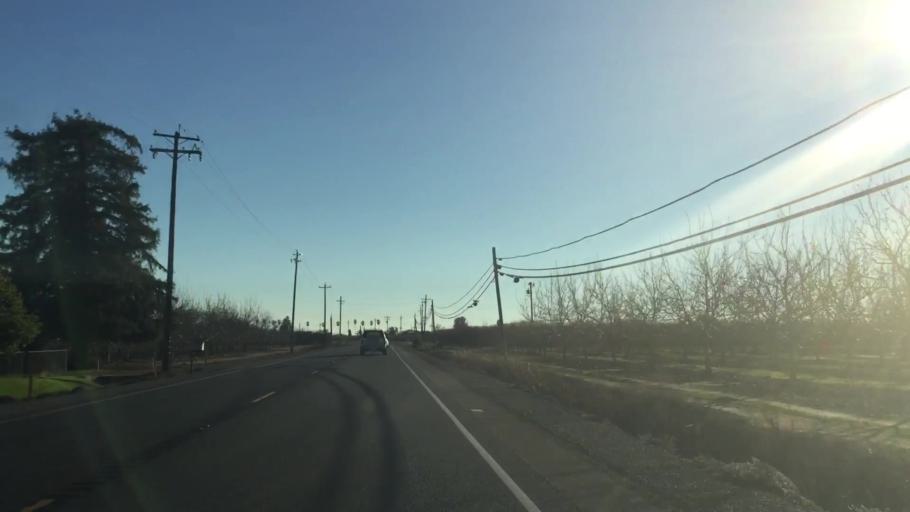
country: US
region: California
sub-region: Yuba County
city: Marysville
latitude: 39.2233
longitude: -121.6012
